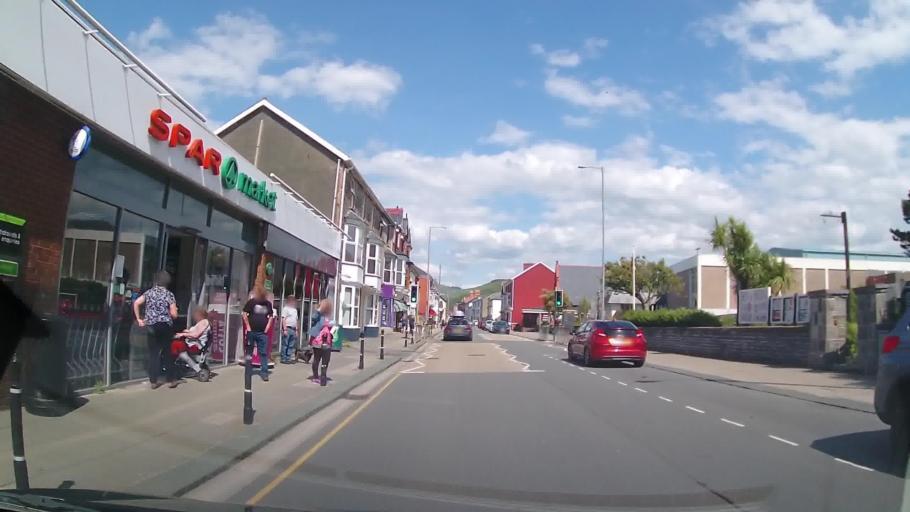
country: GB
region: Wales
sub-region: Gwynedd
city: Tywyn
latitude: 52.5862
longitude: -4.0911
